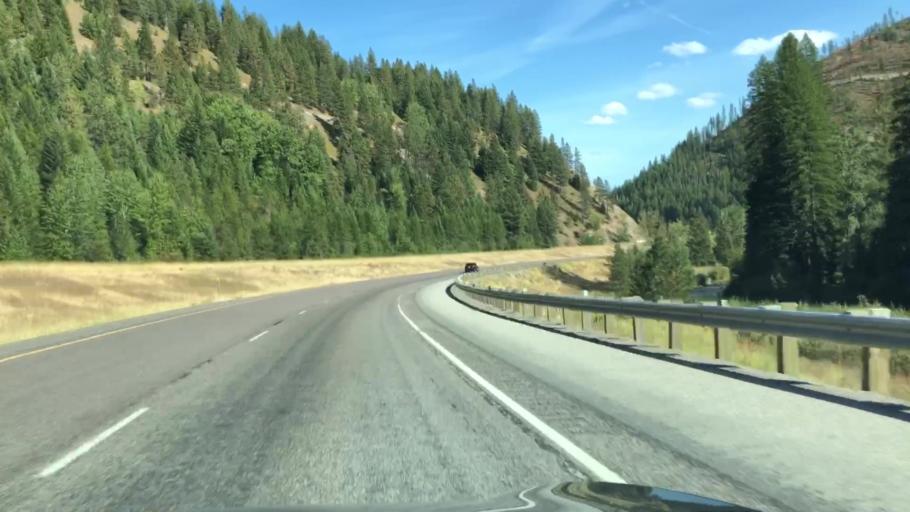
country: US
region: Montana
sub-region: Sanders County
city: Thompson Falls
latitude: 47.4039
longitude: -115.4779
